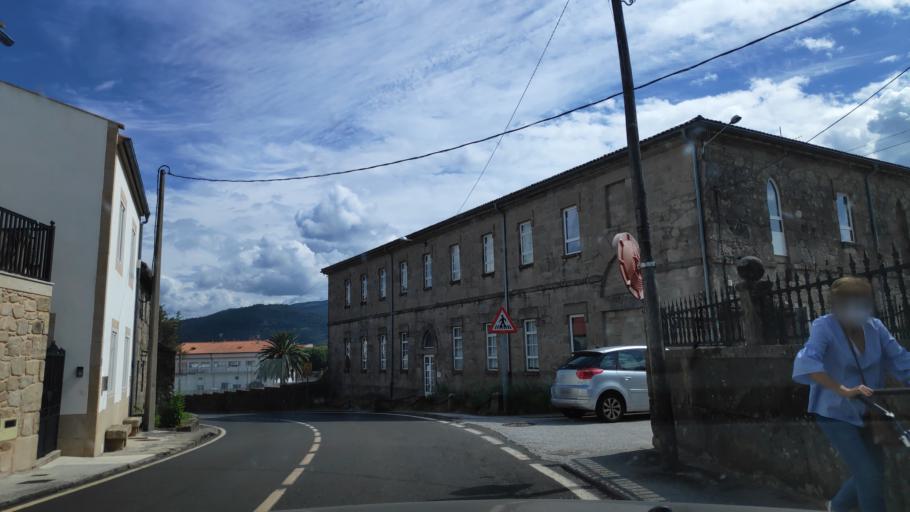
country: ES
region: Galicia
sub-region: Provincia da Coruna
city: Padron
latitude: 42.7364
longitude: -8.6644
